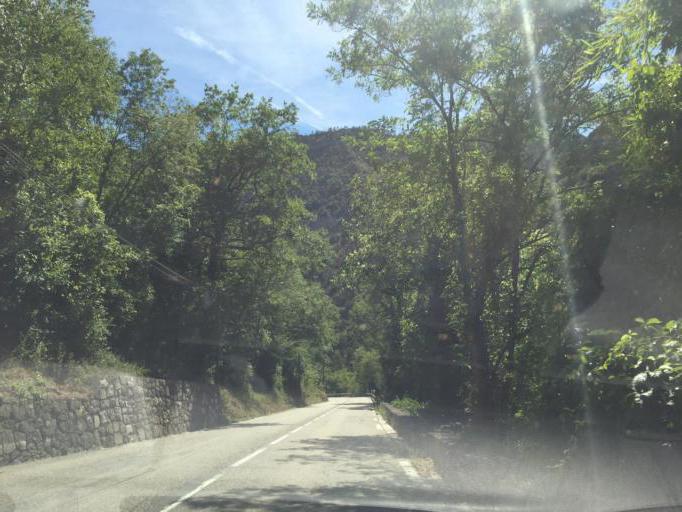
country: FR
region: Provence-Alpes-Cote d'Azur
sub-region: Departement des Alpes-Maritimes
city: Gilette
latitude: 43.9426
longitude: 7.1624
